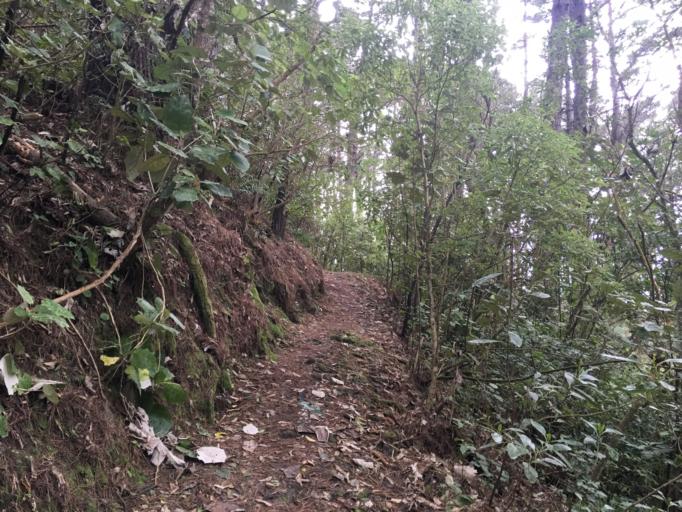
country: NZ
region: Wellington
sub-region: Wellington City
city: Kelburn
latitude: -41.2723
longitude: 174.7707
